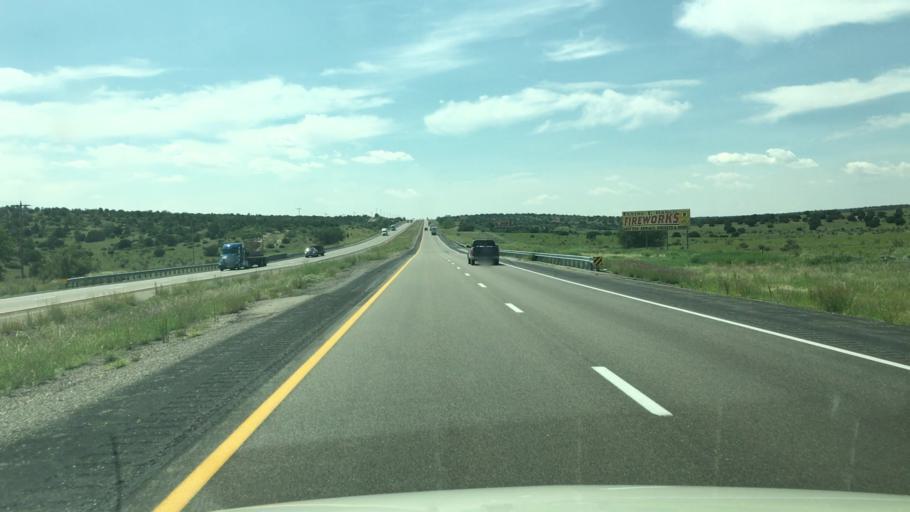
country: US
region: New Mexico
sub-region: San Miguel County
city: Las Vegas
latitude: 34.9921
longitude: -105.3042
